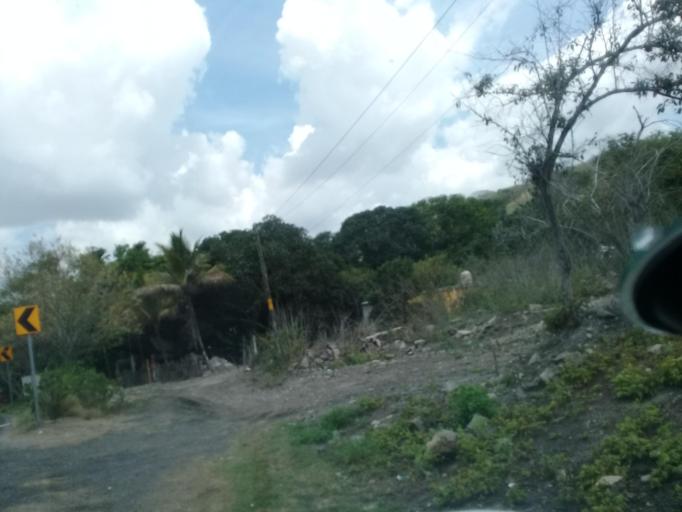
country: MX
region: Veracruz
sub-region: Emiliano Zapata
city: Plan del Rio
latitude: 19.4049
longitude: -96.6513
